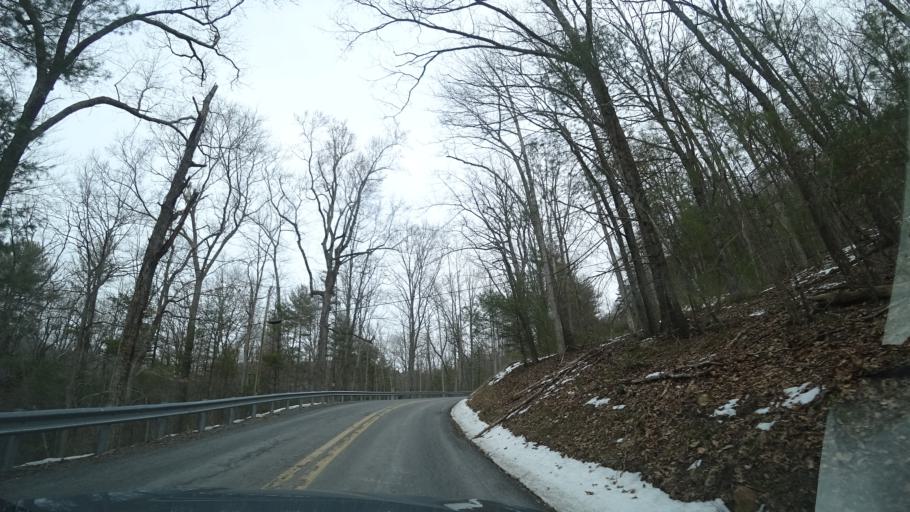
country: US
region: Virginia
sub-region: Shenandoah County
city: Woodstock
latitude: 39.0247
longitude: -78.6629
